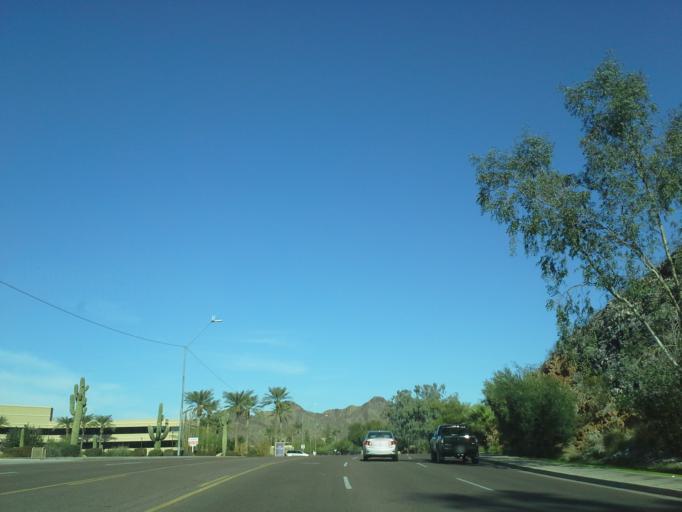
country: US
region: Arizona
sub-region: Maricopa County
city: Phoenix
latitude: 33.5494
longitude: -112.0480
